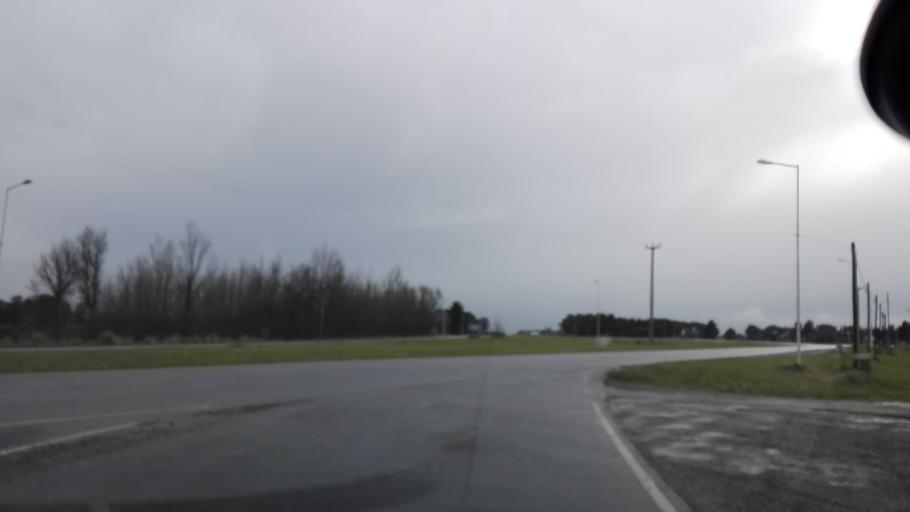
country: AR
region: Buenos Aires
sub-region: Partido de Tandil
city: Tandil
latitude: -37.3484
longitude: -59.1985
